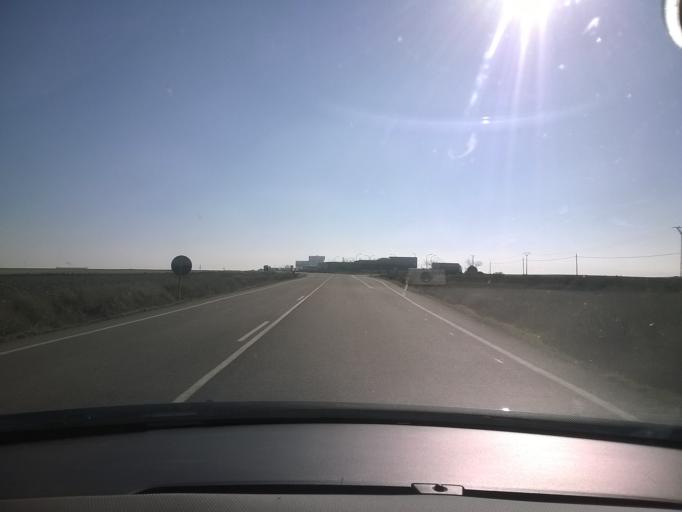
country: ES
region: Aragon
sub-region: Provincia de Zaragoza
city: Bujaraloz
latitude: 41.4876
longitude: -0.1515
